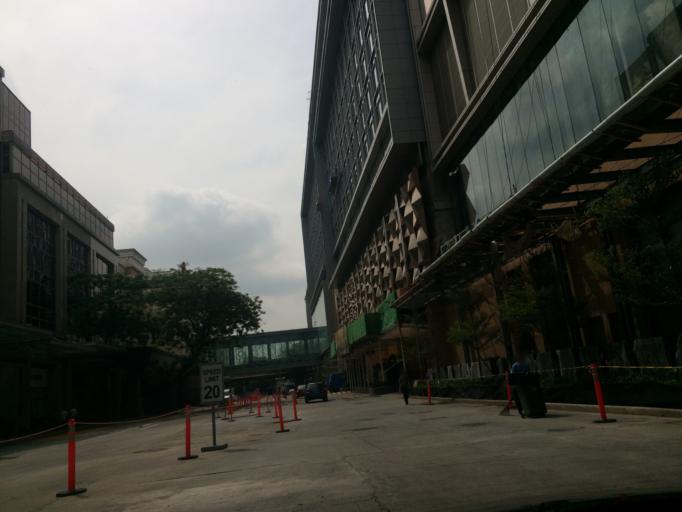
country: PH
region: Metro Manila
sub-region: Makati City
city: Makati City
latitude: 14.5197
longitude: 121.0184
